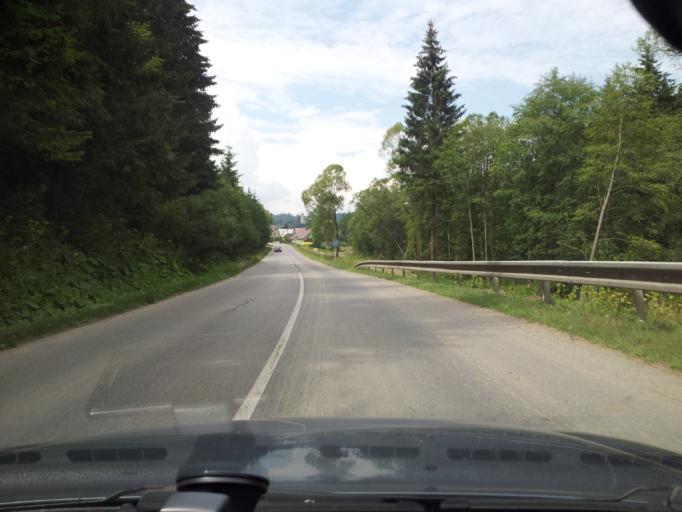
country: SK
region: Zilinsky
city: Oravska Lesna
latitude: 49.3826
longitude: 19.3114
